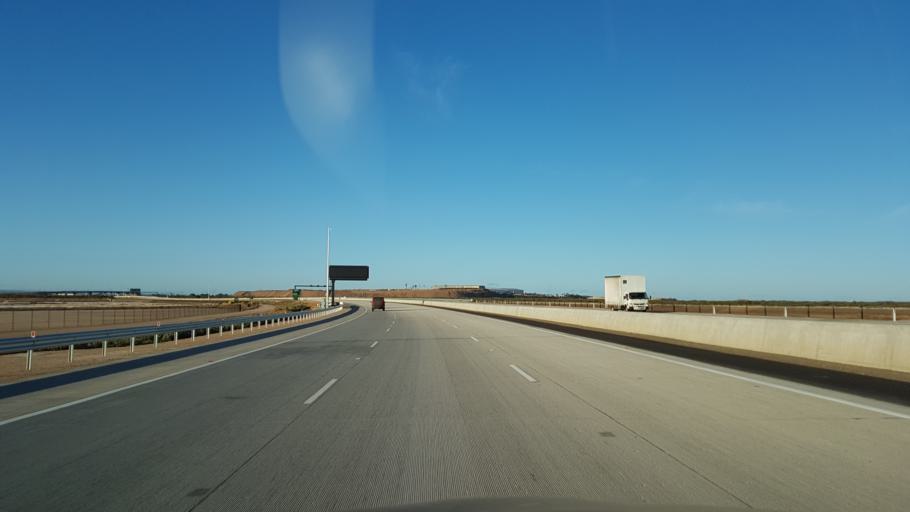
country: AU
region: South Australia
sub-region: Port Adelaide Enfield
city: Enfield
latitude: -34.8134
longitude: 138.5632
